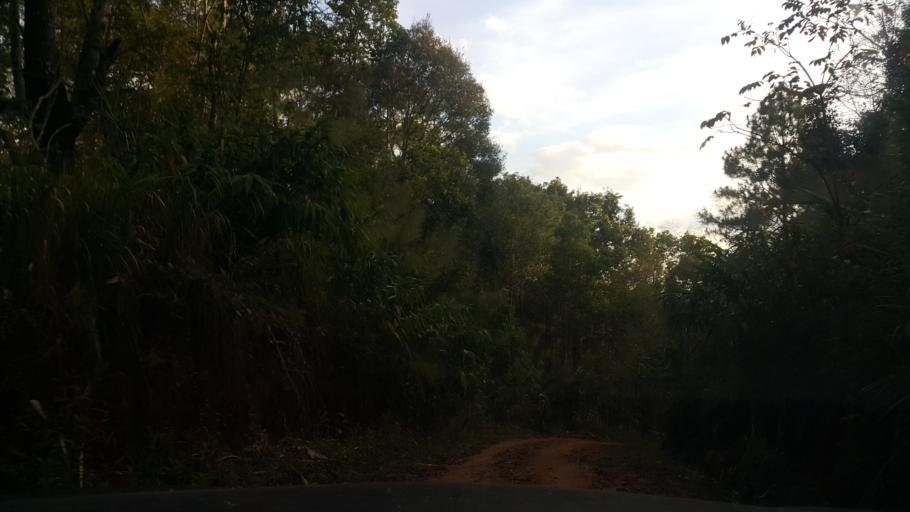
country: TH
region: Chiang Mai
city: Samoeng
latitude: 19.0128
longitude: 98.6502
